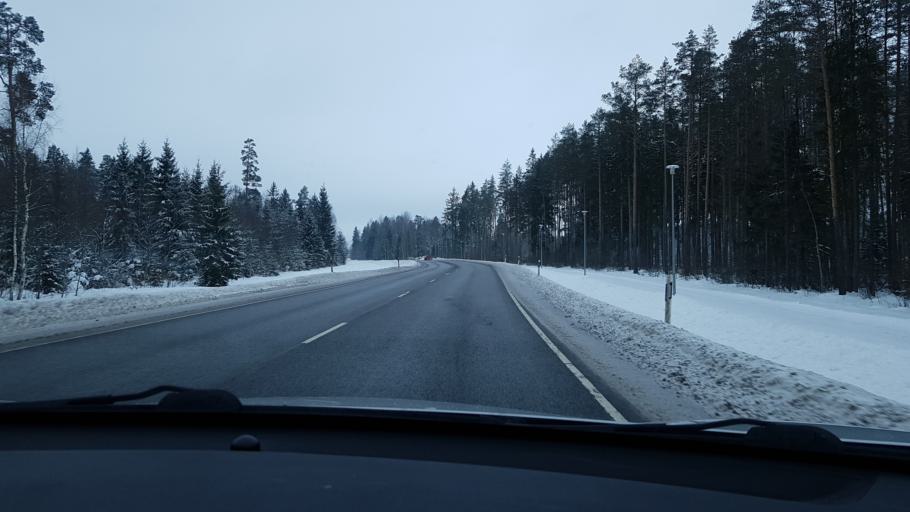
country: EE
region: Jaervamaa
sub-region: Paide linn
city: Paide
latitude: 58.8621
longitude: 25.4905
